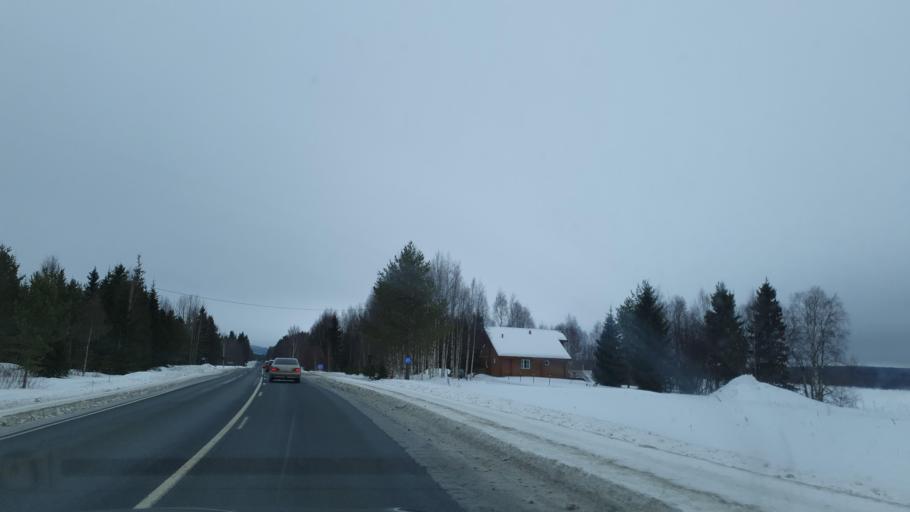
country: FI
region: Lapland
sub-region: Torniolaakso
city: Pello
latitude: 66.6093
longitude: 23.8876
